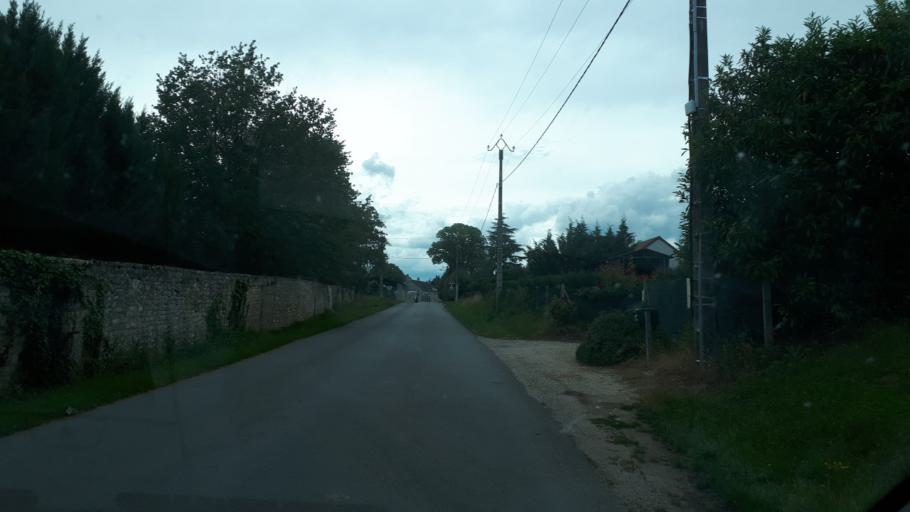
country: FR
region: Centre
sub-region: Departement de l'Indre
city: Reuilly
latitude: 47.0890
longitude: 2.0335
